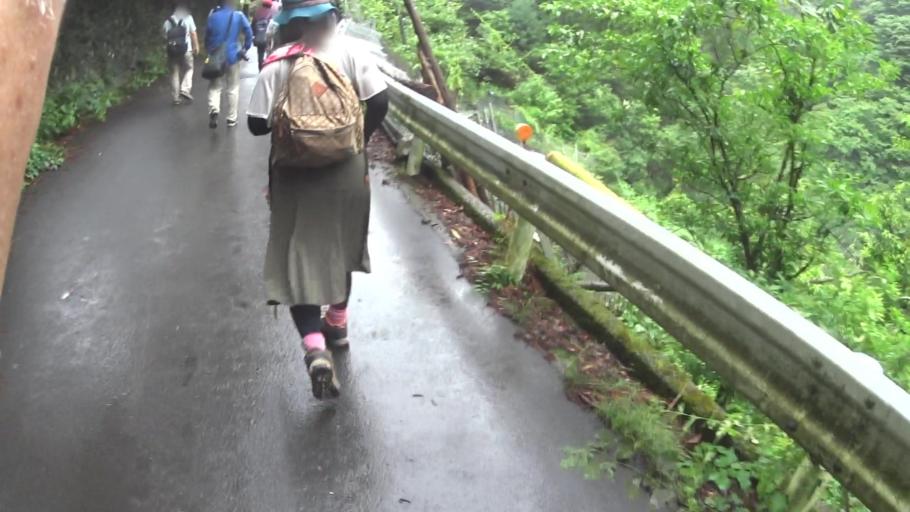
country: JP
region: Tokyo
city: Itsukaichi
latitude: 35.7932
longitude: 139.0730
